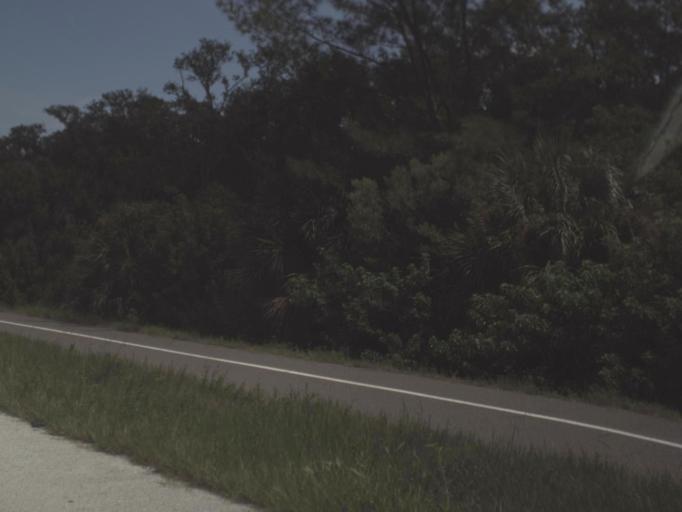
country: US
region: Florida
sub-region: Pinellas County
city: Tierra Verde
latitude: 27.6566
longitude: -82.7184
